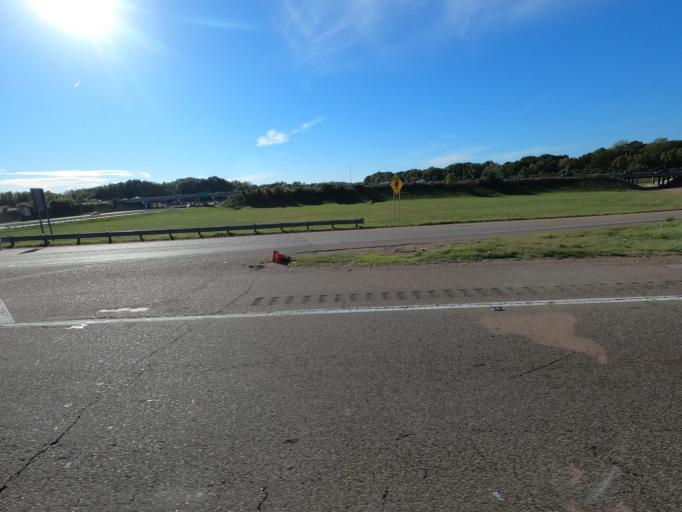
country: US
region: Tennessee
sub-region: Shelby County
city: New South Memphis
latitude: 35.0738
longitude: -90.0256
